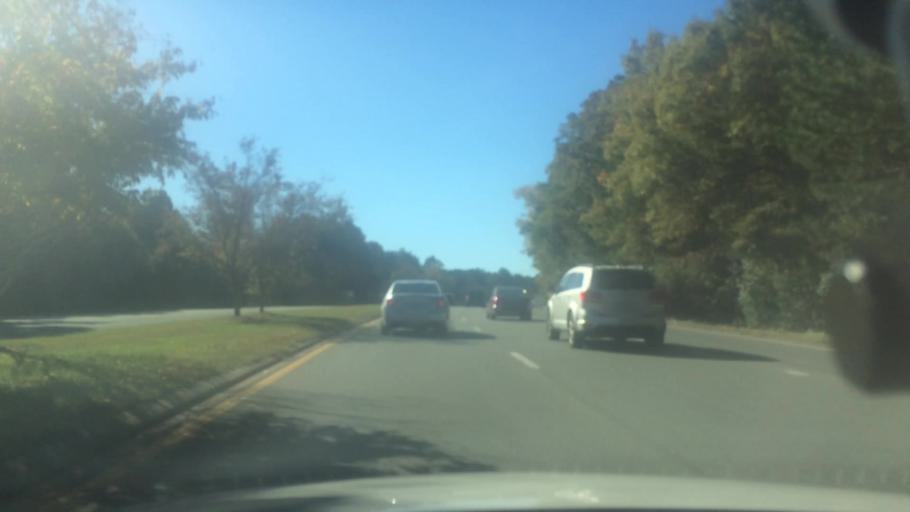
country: US
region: North Carolina
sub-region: Orange County
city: Chapel Hill
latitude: 35.9115
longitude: -79.0266
